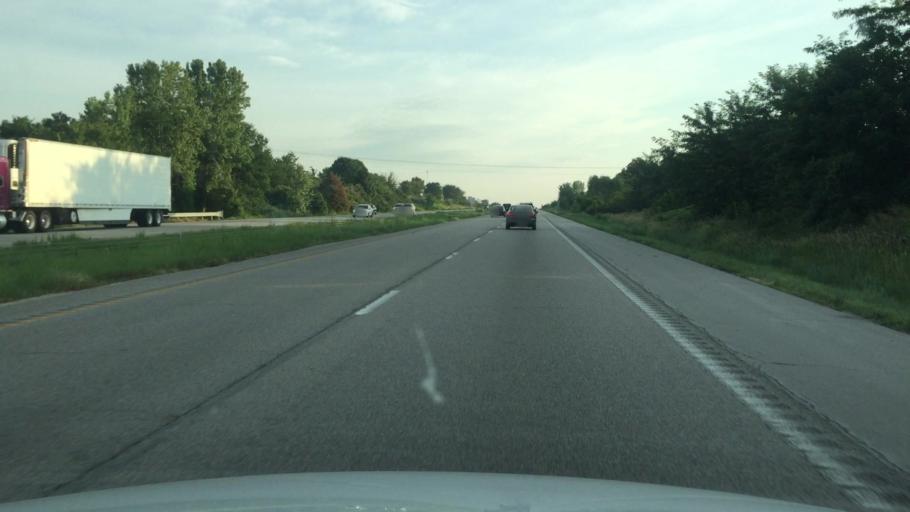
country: US
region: Missouri
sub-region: Platte County
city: Platte City
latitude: 39.3956
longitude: -94.7894
